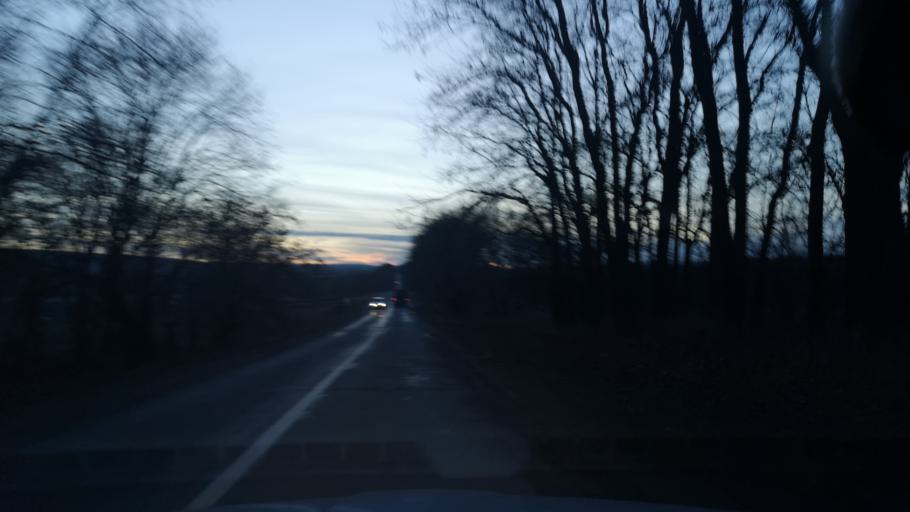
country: MD
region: Orhei
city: Orhei
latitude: 47.2929
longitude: 28.8932
